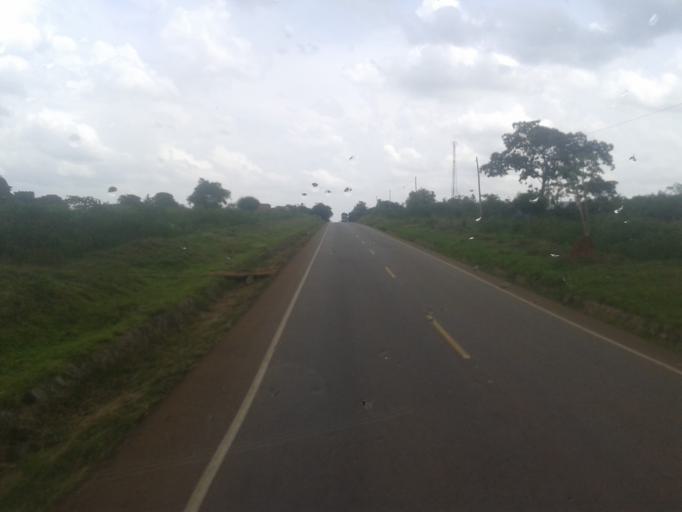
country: UG
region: Central Region
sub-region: Nakasongola District
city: Nakasongola
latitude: 1.3534
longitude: 32.3786
